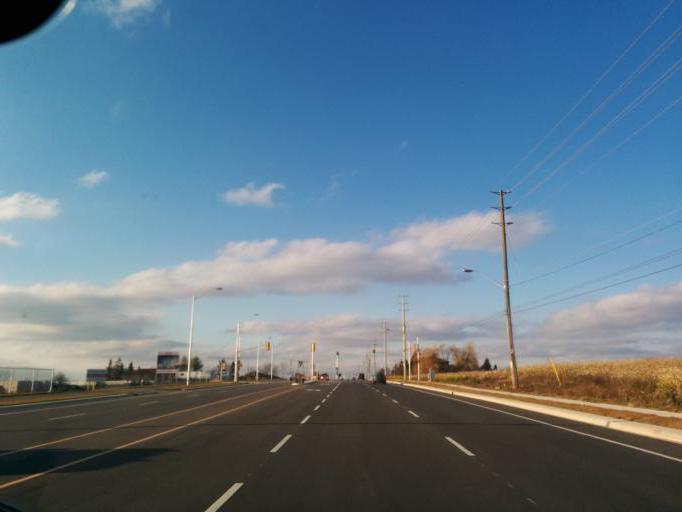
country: CA
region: Ontario
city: Oakville
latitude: 43.5051
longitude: -79.6930
